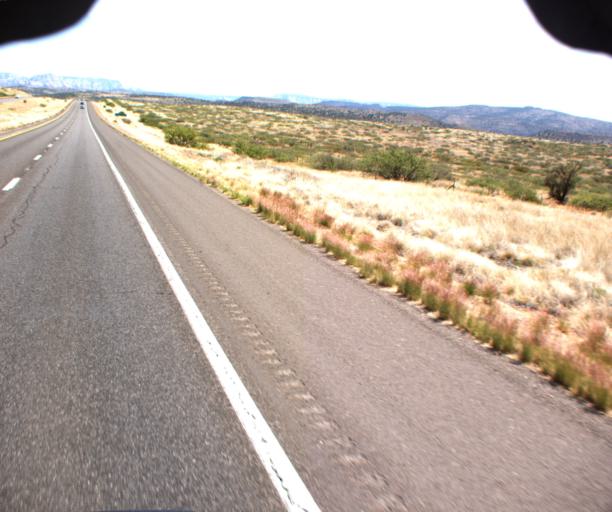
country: US
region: Arizona
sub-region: Yavapai County
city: Cornville
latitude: 34.7652
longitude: -111.9426
